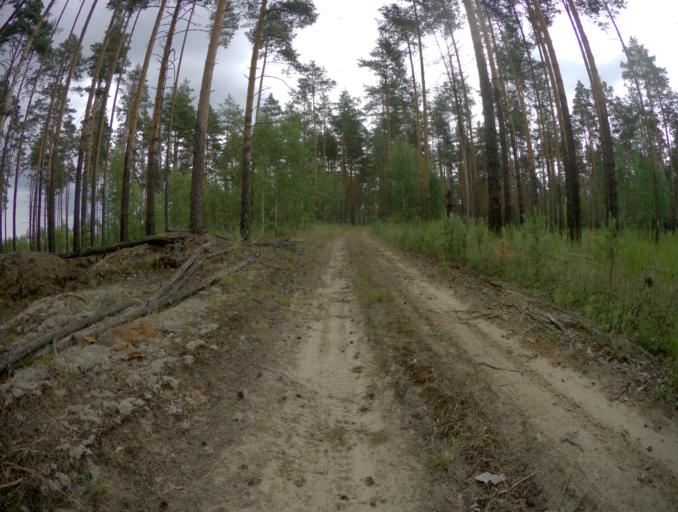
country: RU
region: Nizjnij Novgorod
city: Frolishchi
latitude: 56.3431
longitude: 42.6345
